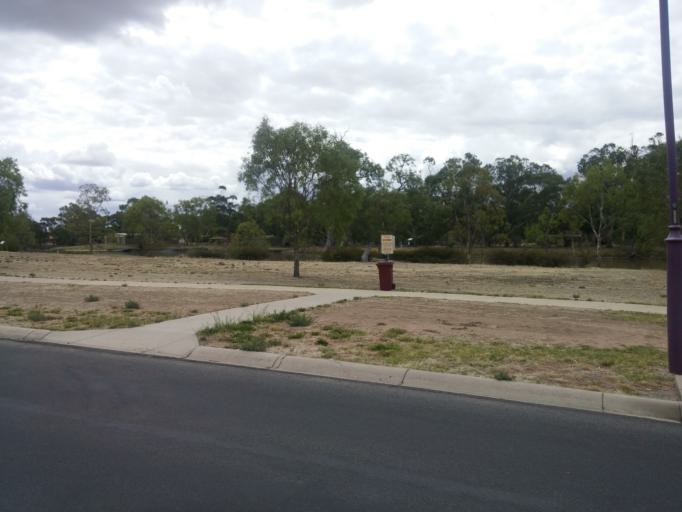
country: AU
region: Victoria
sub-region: Horsham
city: Horsham
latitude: -36.7254
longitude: 142.1981
